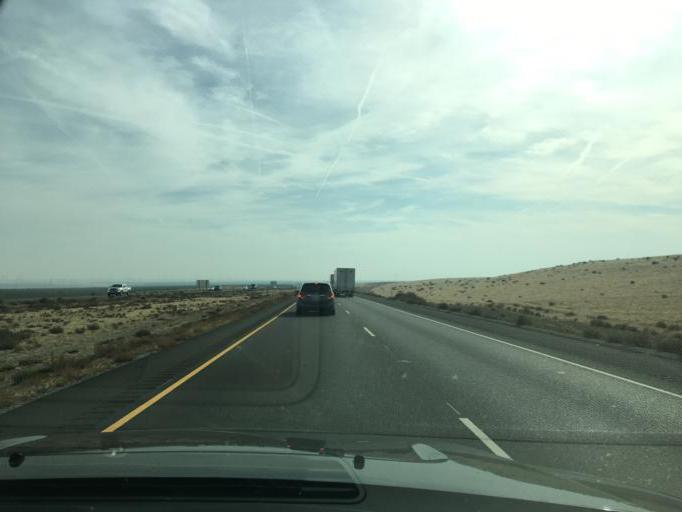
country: US
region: California
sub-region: Kings County
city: Kettleman City
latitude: 35.9675
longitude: -119.9460
